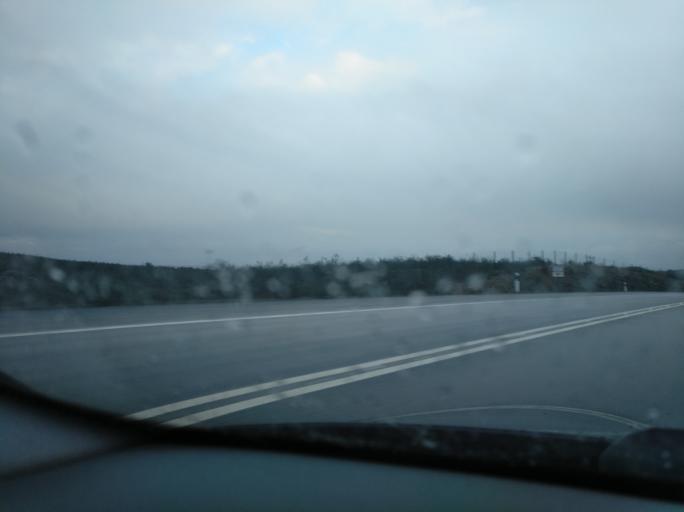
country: PT
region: Faro
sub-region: Alcoutim
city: Alcoutim
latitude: 37.3725
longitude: -7.5232
